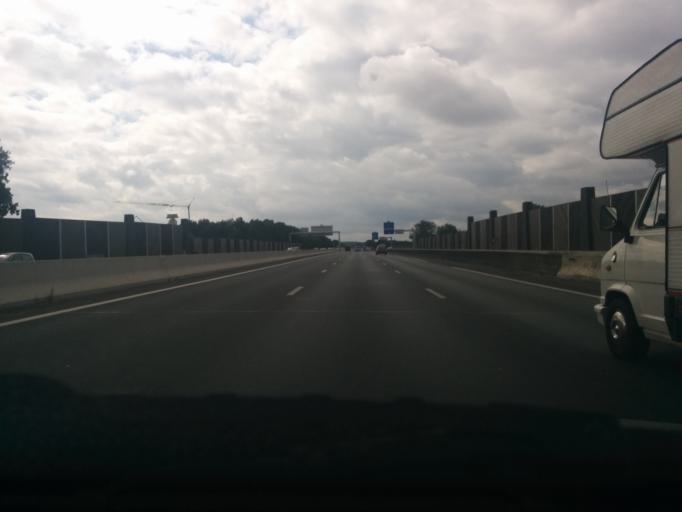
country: FR
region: Pays de la Loire
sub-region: Departement de Maine-et-Loire
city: Les Ponts-de-Ce
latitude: 47.4371
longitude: -0.5098
